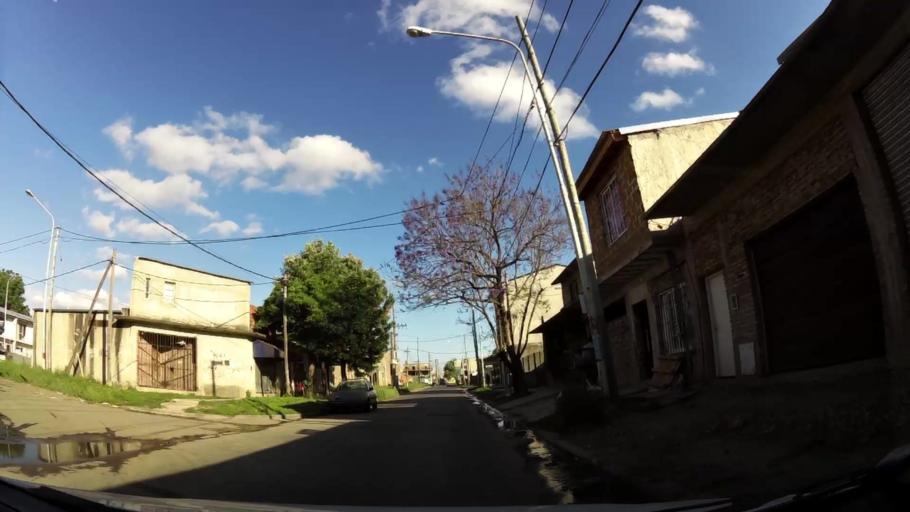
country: AR
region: Buenos Aires
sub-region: Partido de Moron
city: Moron
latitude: -34.6820
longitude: -58.6210
